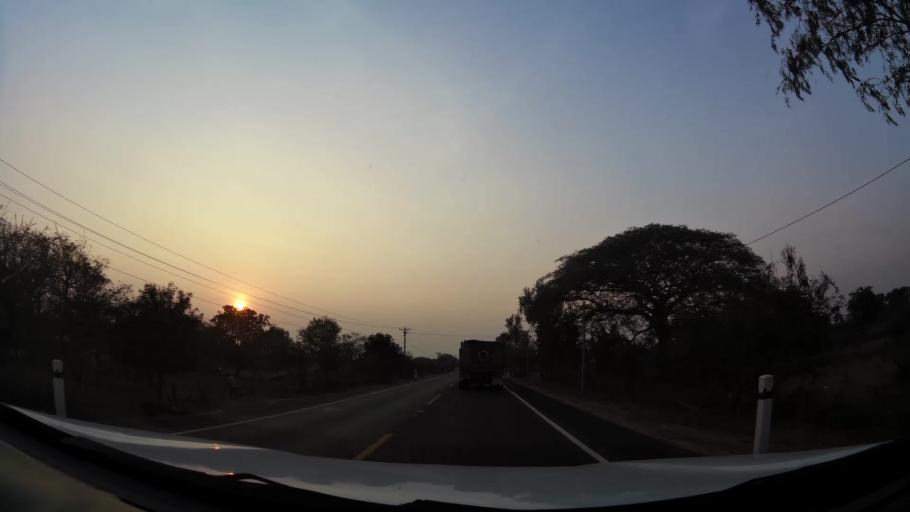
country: NI
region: Leon
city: La Paz Centro
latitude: 12.3044
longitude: -86.7768
